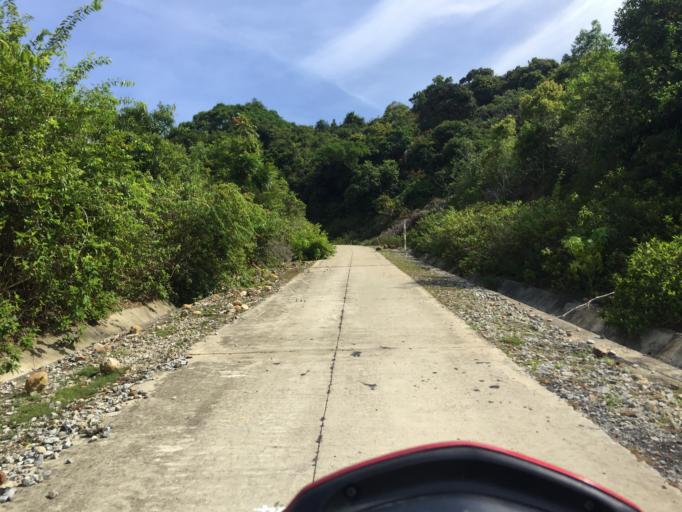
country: VN
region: Quang Nam
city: Hoi An
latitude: 15.9378
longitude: 108.5332
